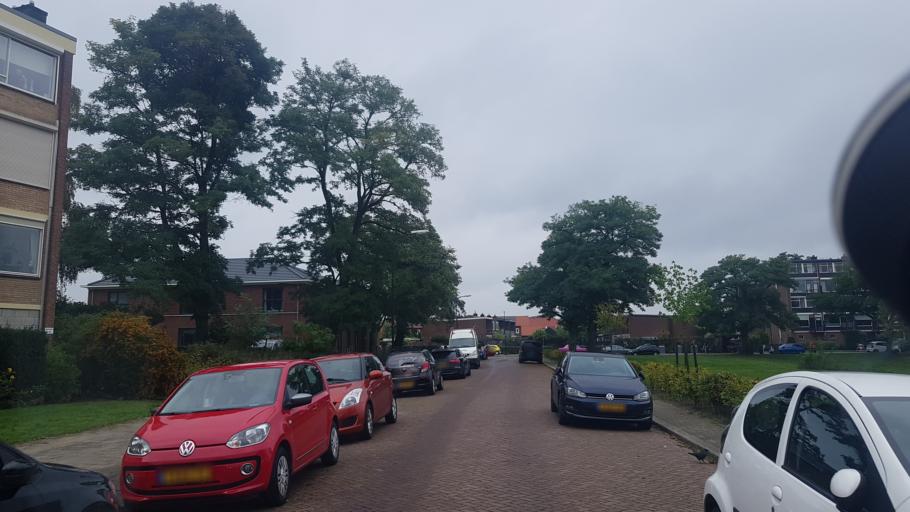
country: NL
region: Gelderland
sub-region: Gemeente Apeldoorn
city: Apeldoorn
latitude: 52.1964
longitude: 5.9716
